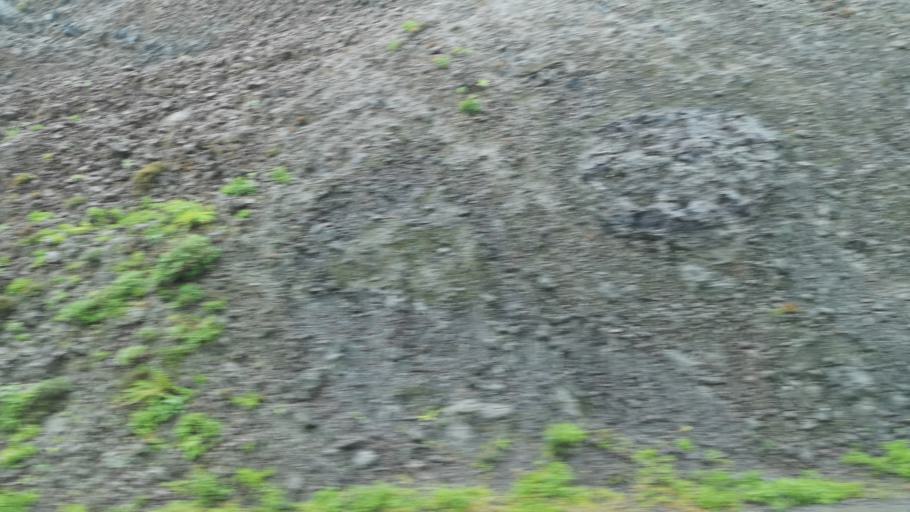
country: ES
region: Canary Islands
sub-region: Provincia de Santa Cruz de Tenerife
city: Alajero
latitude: 28.0892
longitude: -17.1999
